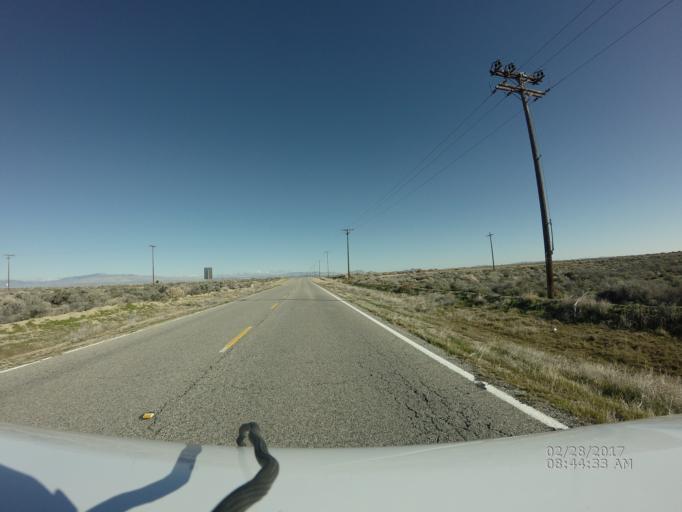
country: US
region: California
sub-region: Los Angeles County
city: Quartz Hill
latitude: 34.7614
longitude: -118.2372
